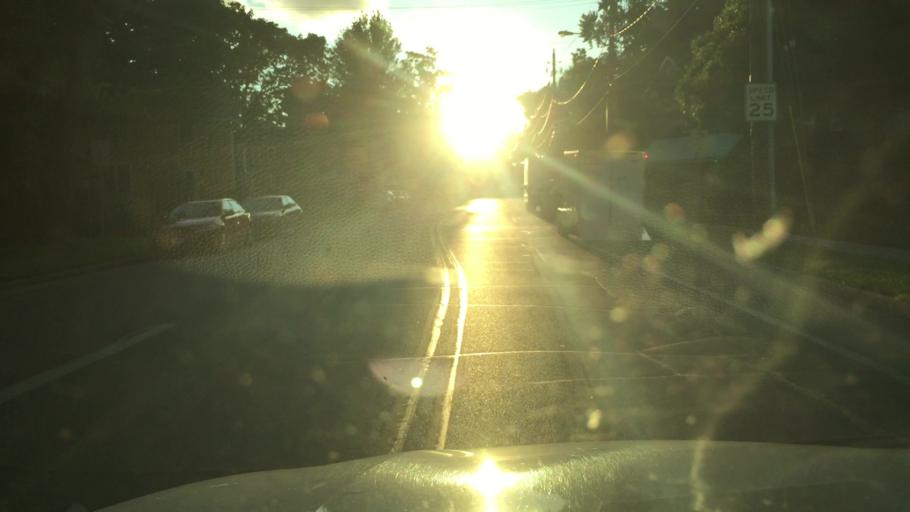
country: US
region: Iowa
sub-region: Polk County
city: Des Moines
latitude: 41.5972
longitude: -93.6511
